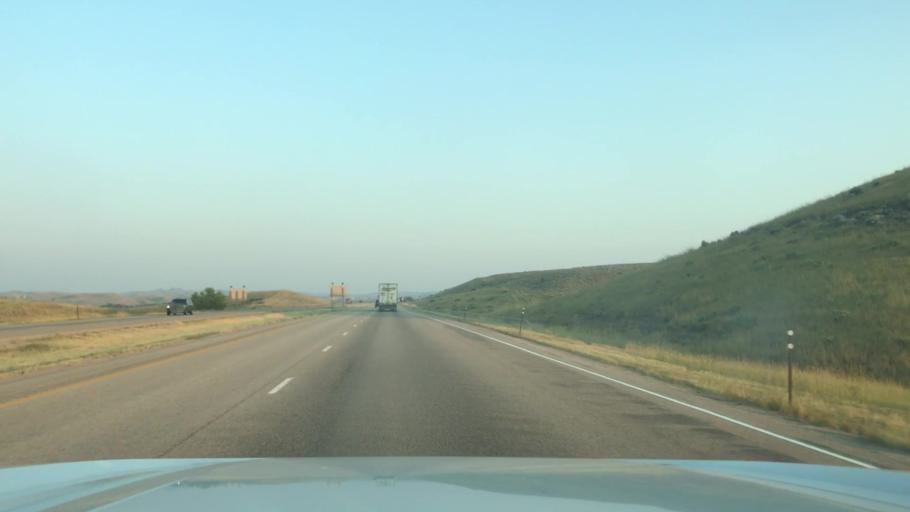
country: US
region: Wyoming
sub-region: Sheridan County
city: Sheridan
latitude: 44.8786
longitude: -107.0007
